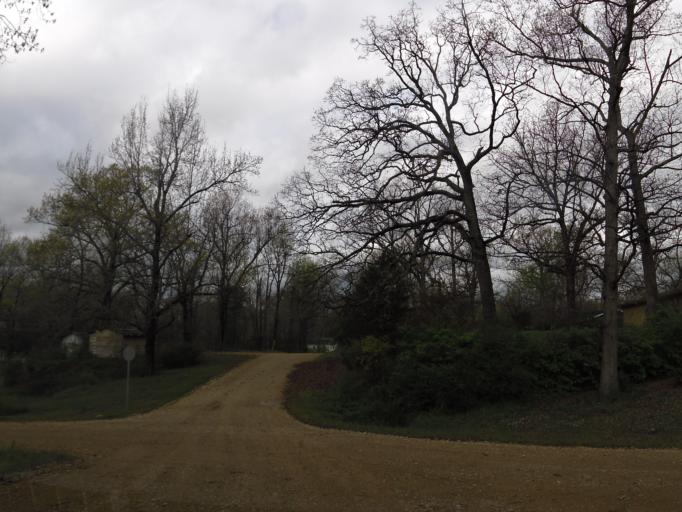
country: US
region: Missouri
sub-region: Butler County
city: Poplar Bluff
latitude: 36.7511
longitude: -90.4033
